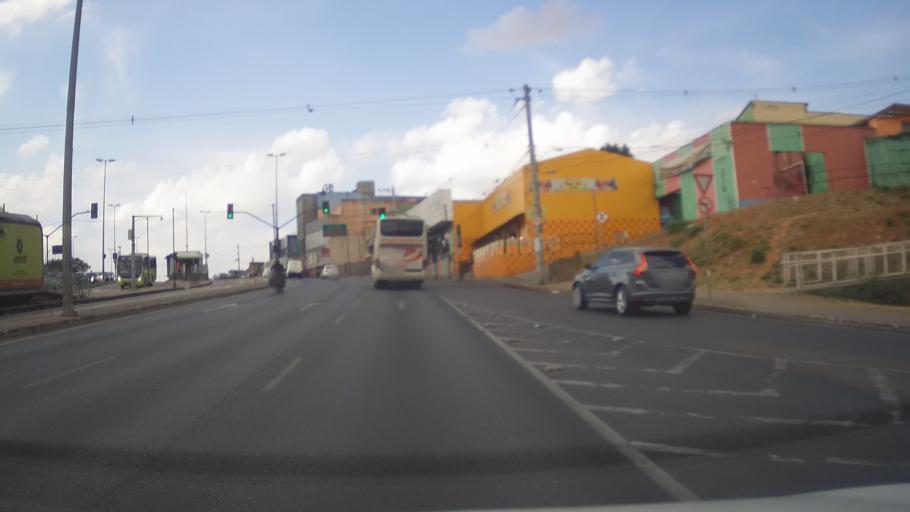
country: BR
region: Minas Gerais
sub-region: Belo Horizonte
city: Belo Horizonte
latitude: -19.8845
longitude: -43.9506
